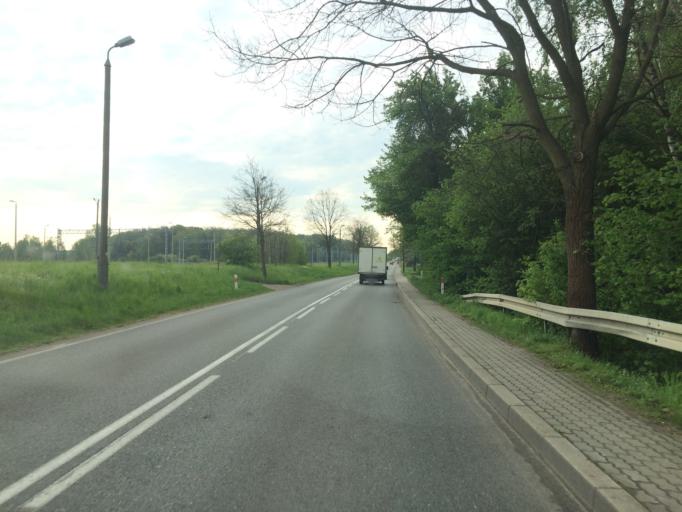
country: PL
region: Warmian-Masurian Voivodeship
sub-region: Powiat dzialdowski
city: Ilowo -Osada
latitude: 53.1612
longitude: 20.3015
